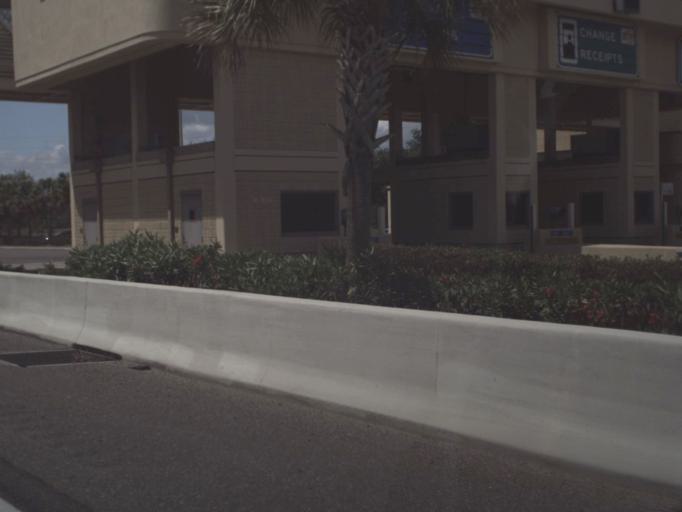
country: US
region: Florida
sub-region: Orange County
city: Oakland
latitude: 28.4993
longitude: -81.6169
